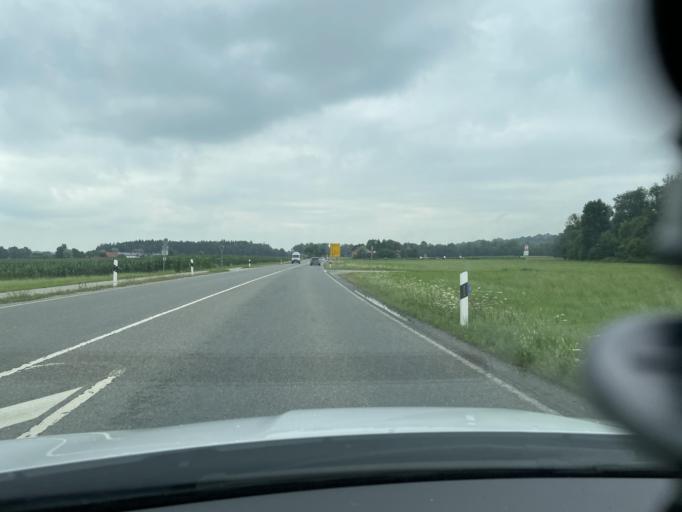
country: DE
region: Bavaria
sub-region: Upper Bavaria
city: Ramerberg
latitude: 47.9966
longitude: 12.1522
